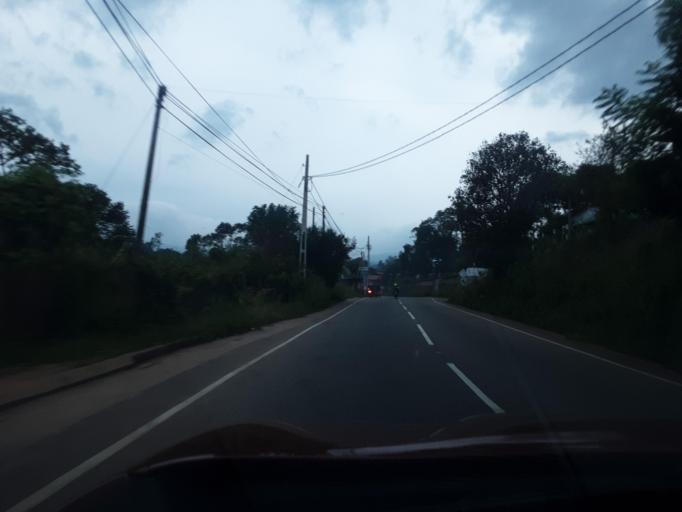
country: LK
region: Central
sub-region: Nuwara Eliya District
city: Nuwara Eliya
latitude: 6.9015
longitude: 80.8999
